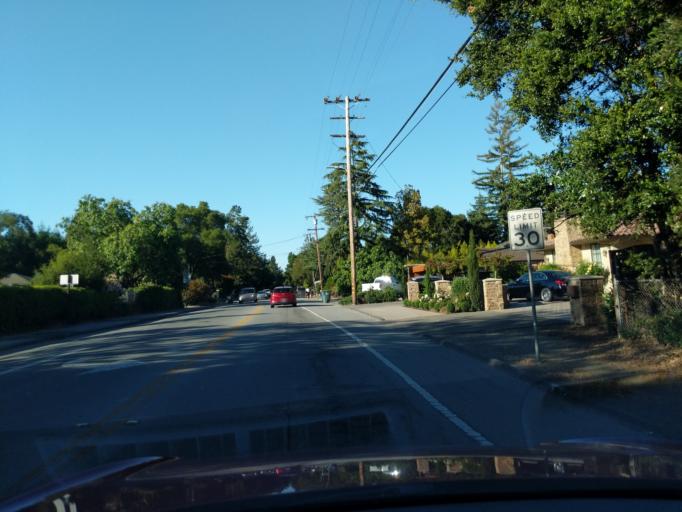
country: US
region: California
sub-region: San Mateo County
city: West Menlo Park
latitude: 37.4355
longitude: -122.1980
